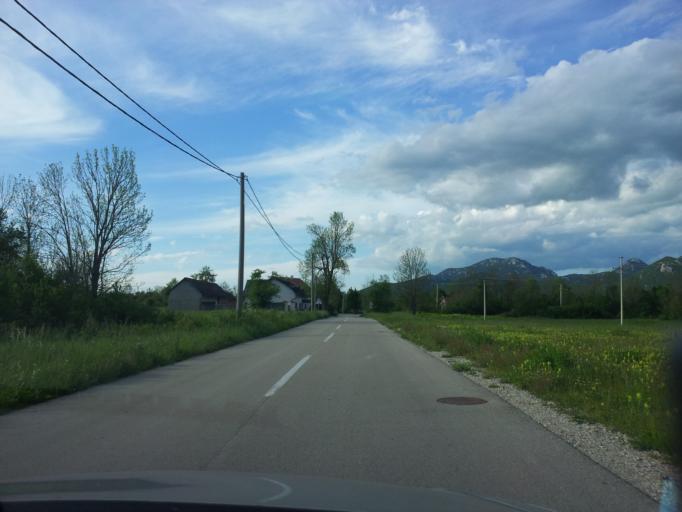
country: HR
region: Zadarska
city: Obrovac
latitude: 44.3863
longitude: 15.6784
